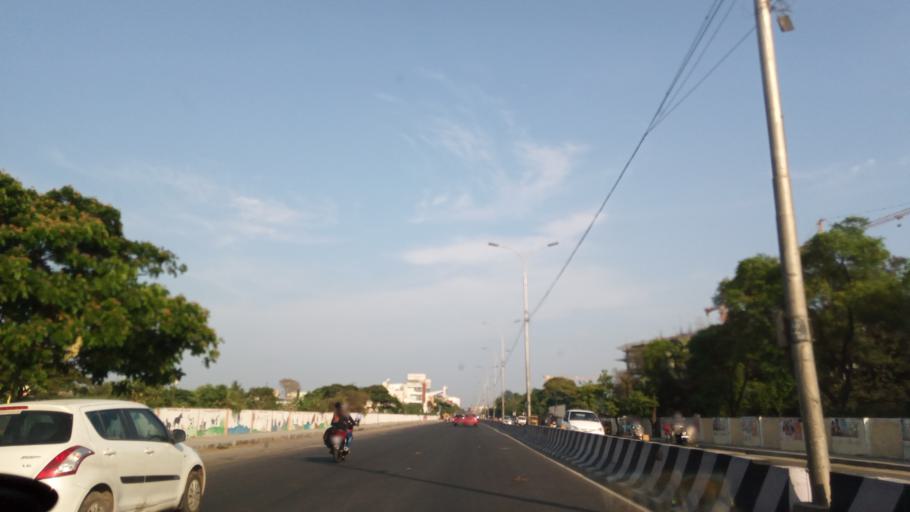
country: IN
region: Tamil Nadu
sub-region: Thiruvallur
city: Porur
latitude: 13.0276
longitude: 80.1720
